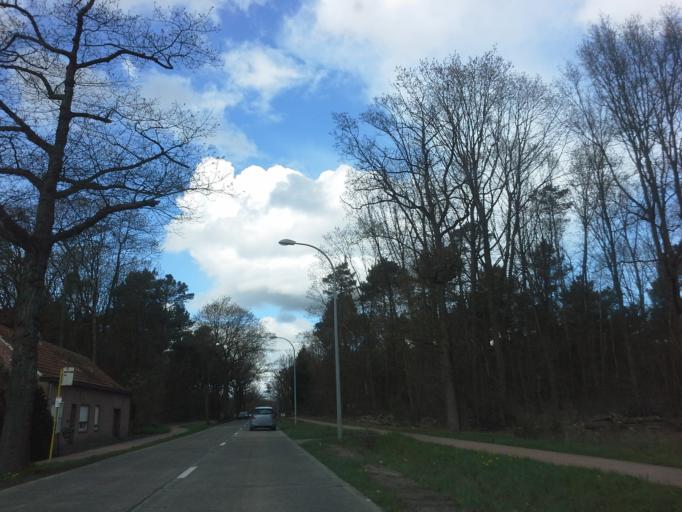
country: BE
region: Flanders
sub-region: Provincie Antwerpen
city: Meerhout
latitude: 51.1403
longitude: 5.0579
